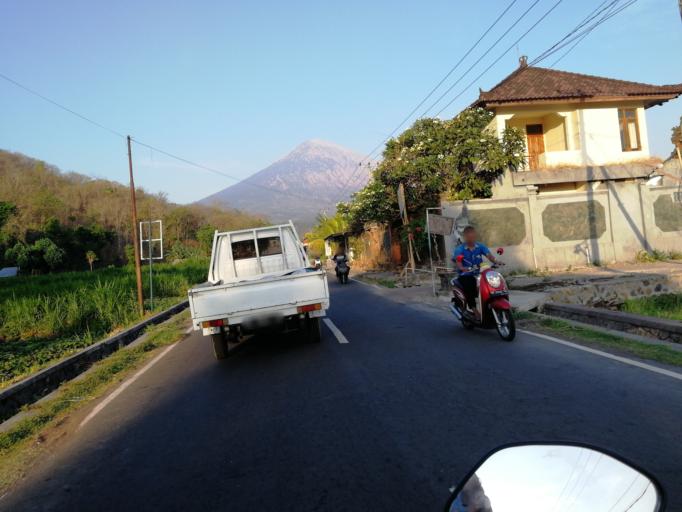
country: ID
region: Bali
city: Biaslantang Kaler
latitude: -8.3366
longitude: 115.6257
